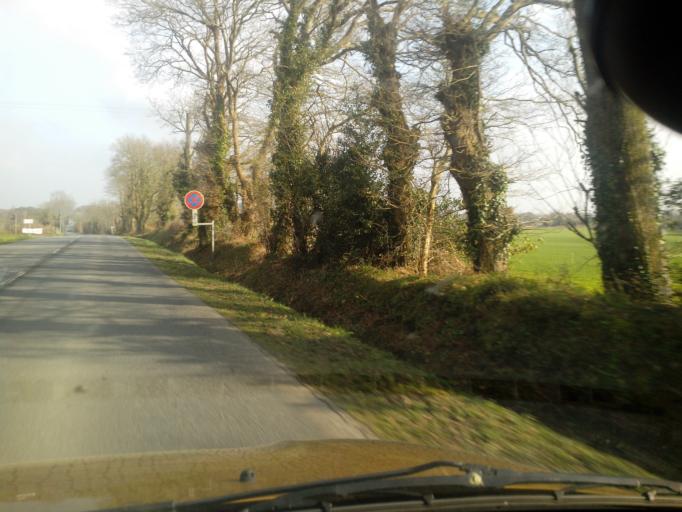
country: FR
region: Brittany
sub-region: Departement du Morbihan
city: Questembert
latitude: 47.6897
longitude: -2.4733
